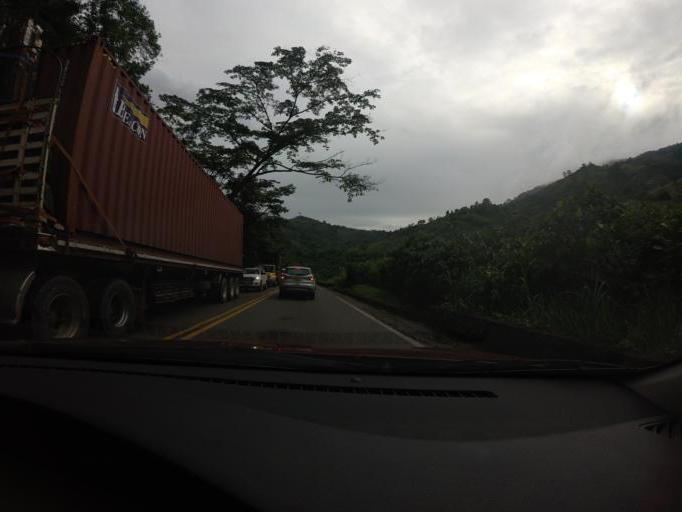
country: CO
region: Cundinamarca
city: Villeta
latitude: 5.0225
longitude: -74.5221
